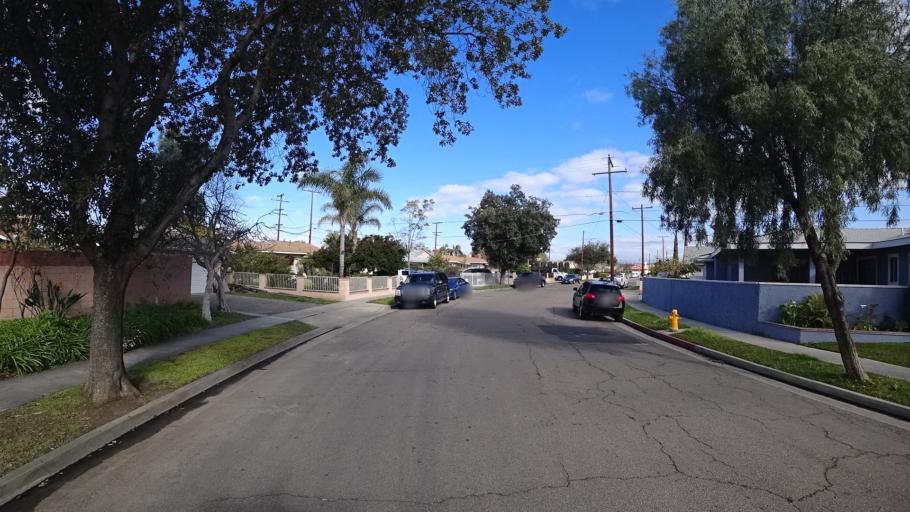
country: US
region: California
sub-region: Orange County
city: Anaheim
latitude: 33.8520
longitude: -117.9018
